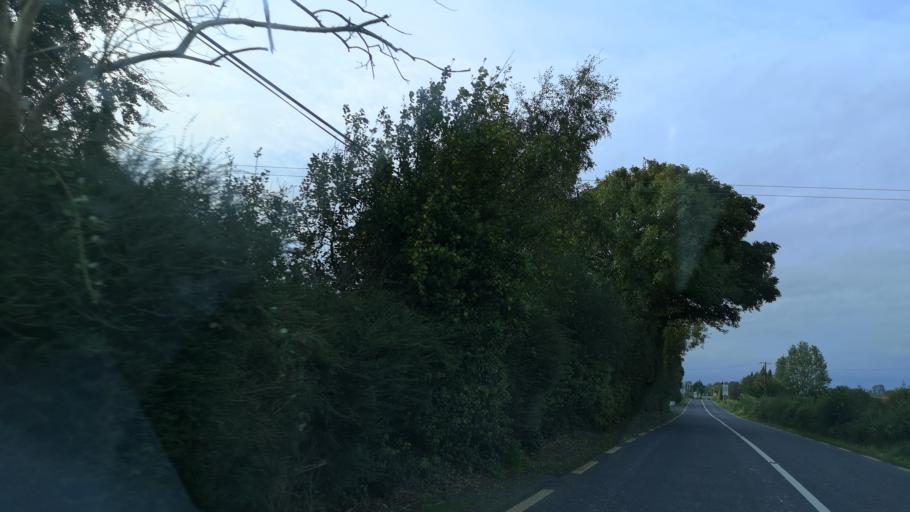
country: IE
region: Leinster
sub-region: Uibh Fhaili
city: Ferbane
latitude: 53.3262
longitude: -7.8219
